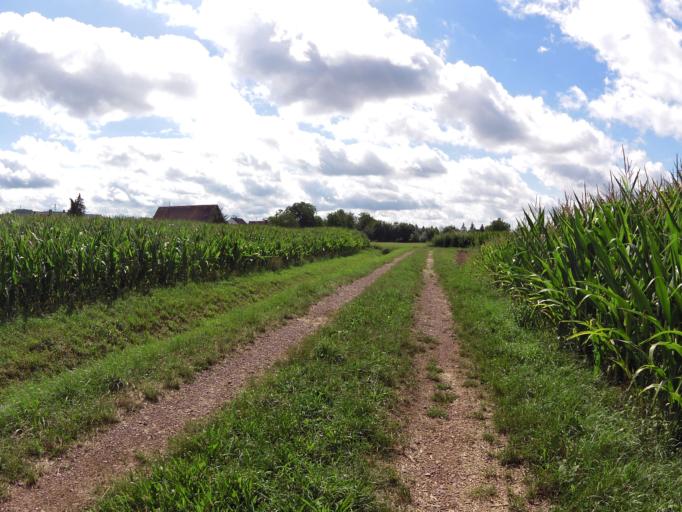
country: DE
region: Baden-Wuerttemberg
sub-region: Freiburg Region
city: Lahr
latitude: 48.3652
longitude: 7.8305
